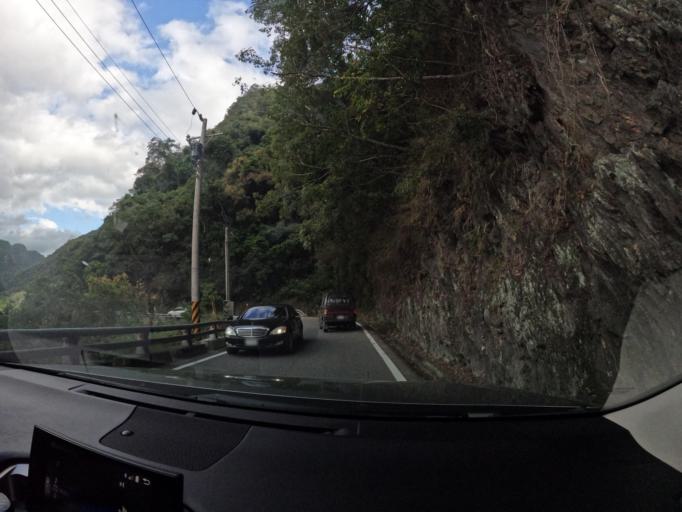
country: TW
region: Taiwan
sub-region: Taitung
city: Taitung
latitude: 23.1401
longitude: 121.0859
